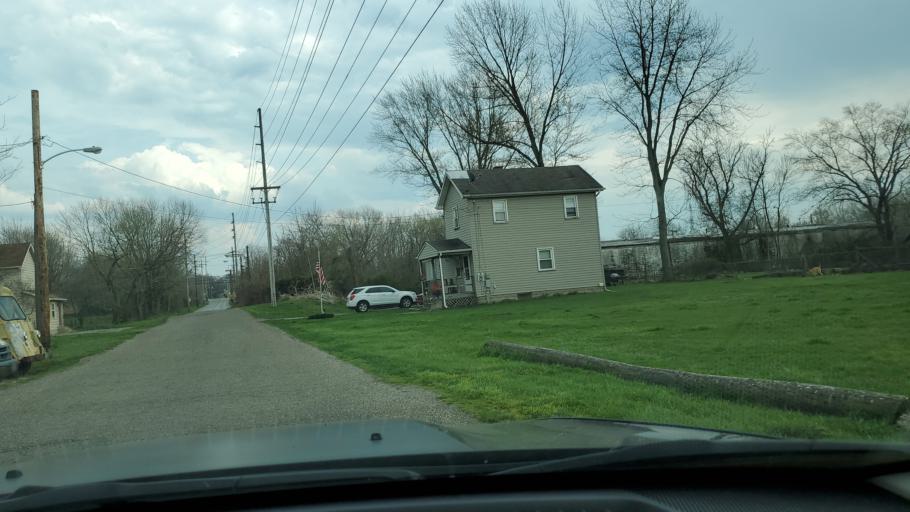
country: US
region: Ohio
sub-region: Trumbull County
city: Niles
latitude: 41.1770
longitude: -80.7594
